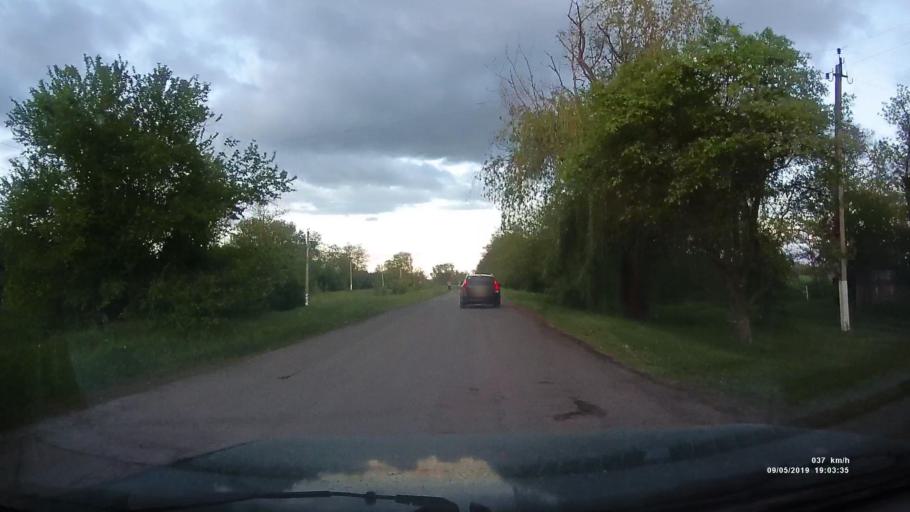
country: RU
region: Krasnodarskiy
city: Kanelovskaya
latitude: 46.7423
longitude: 39.1647
